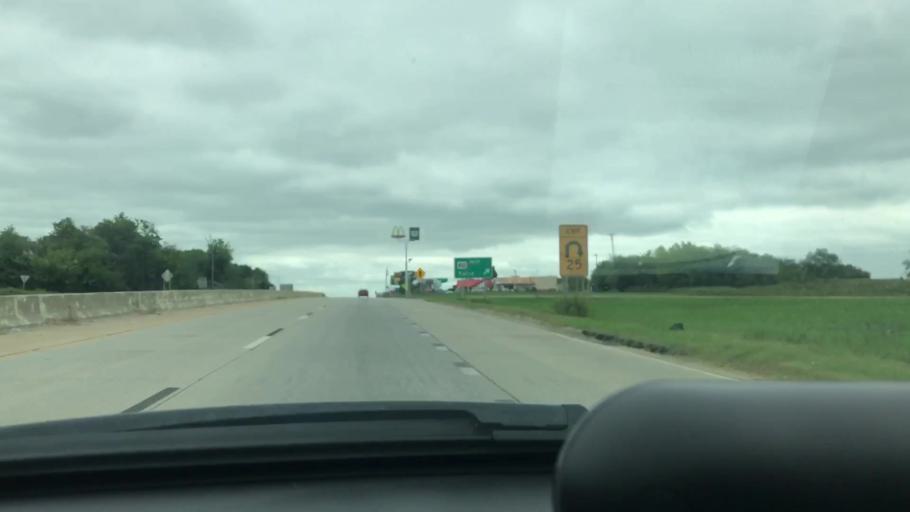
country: US
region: Oklahoma
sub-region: Mayes County
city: Chouteau
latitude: 36.1670
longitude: -95.3418
